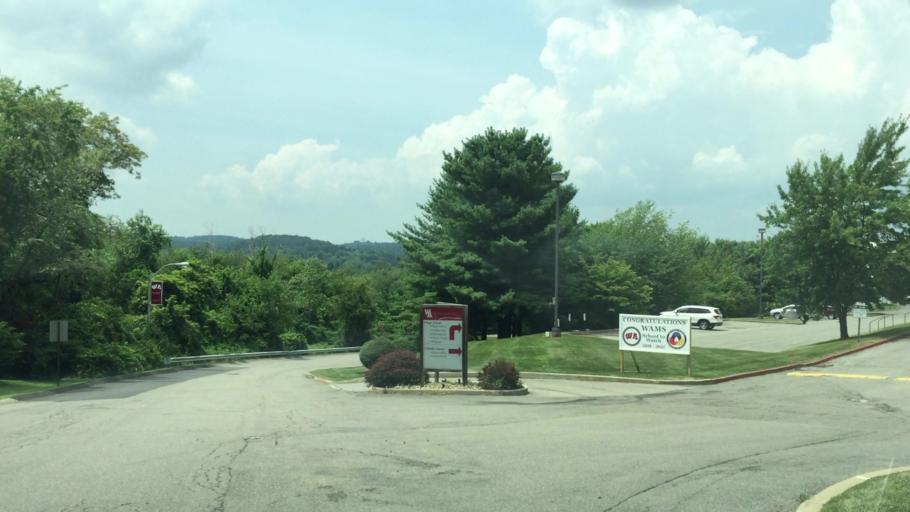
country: US
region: Pennsylvania
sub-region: Allegheny County
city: Imperial
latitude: 40.4461
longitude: -80.2377
